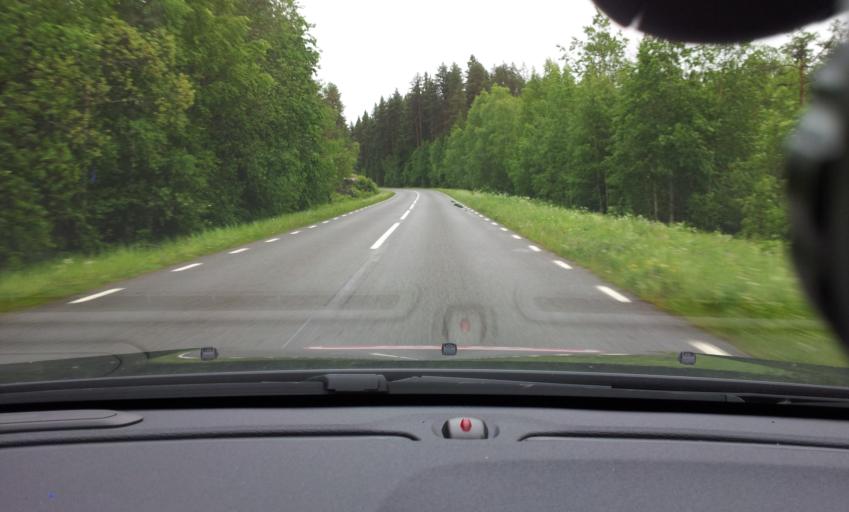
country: SE
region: Jaemtland
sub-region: Stroemsunds Kommun
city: Stroemsund
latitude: 63.4295
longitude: 15.5021
